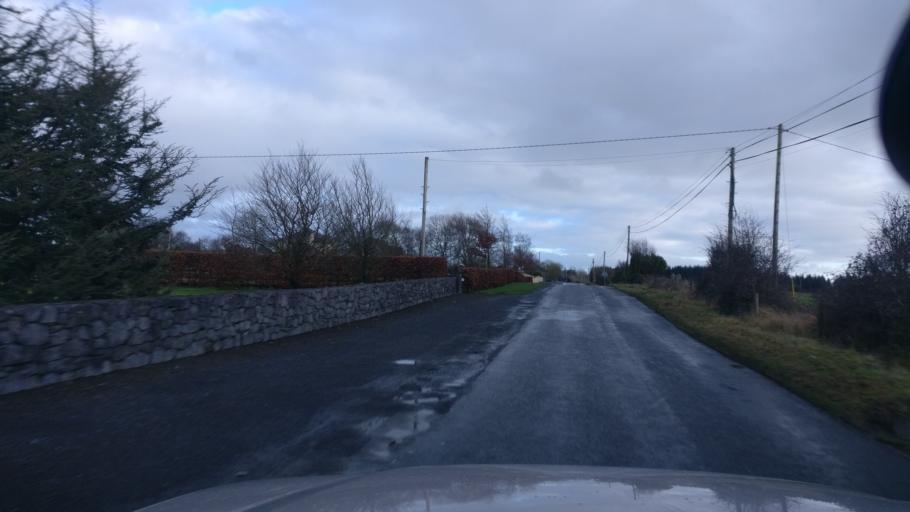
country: IE
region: Connaught
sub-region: County Galway
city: Athenry
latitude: 53.2989
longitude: -8.7127
